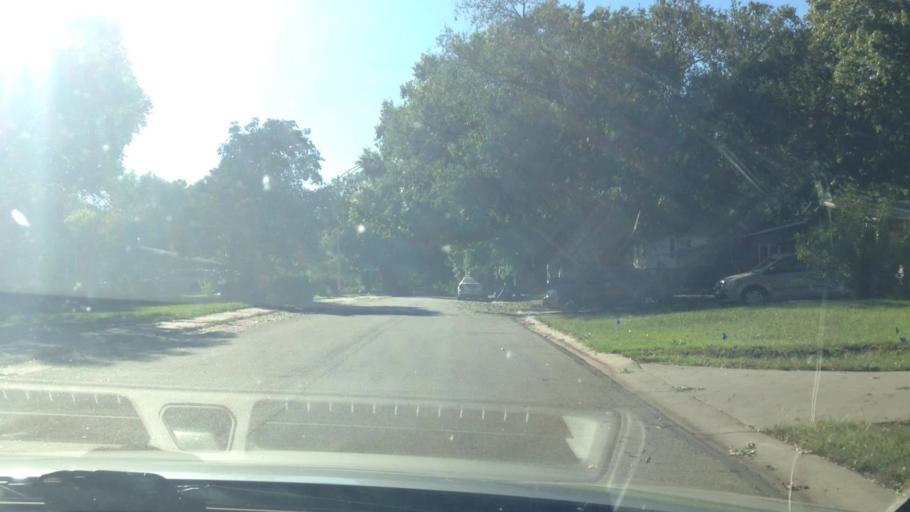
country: US
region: Kansas
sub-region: Johnson County
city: Prairie Village
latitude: 38.9923
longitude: -94.6522
